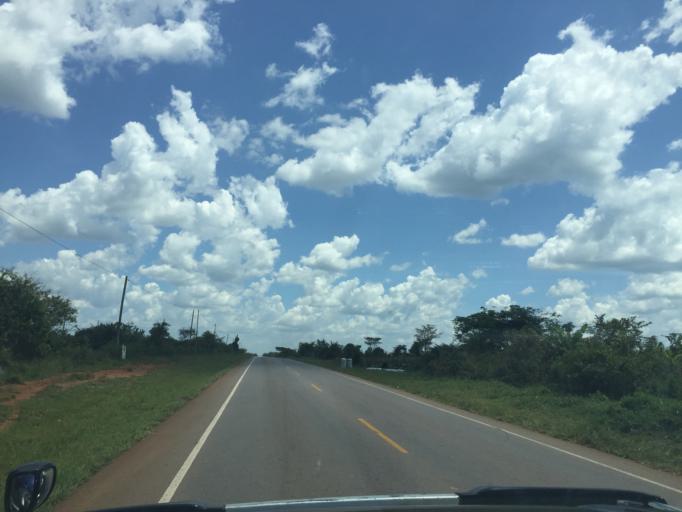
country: UG
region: Central Region
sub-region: Nakasongola District
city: Nakasongola
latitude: 1.3698
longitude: 32.3545
